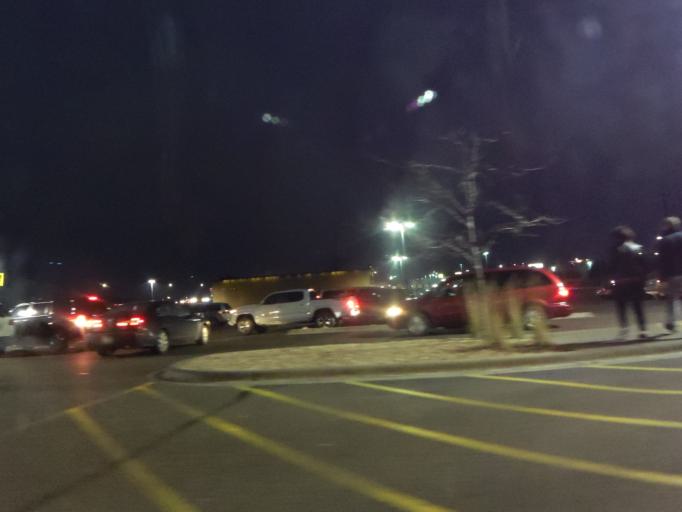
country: US
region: Minnesota
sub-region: Ramsey County
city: North Saint Paul
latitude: 45.0364
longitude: -93.0255
